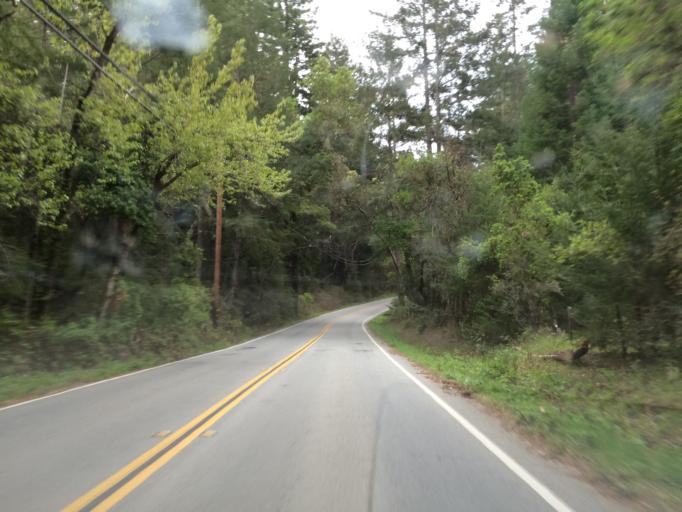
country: US
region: California
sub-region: Santa Cruz County
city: Felton
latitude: 37.0131
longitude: -122.0752
